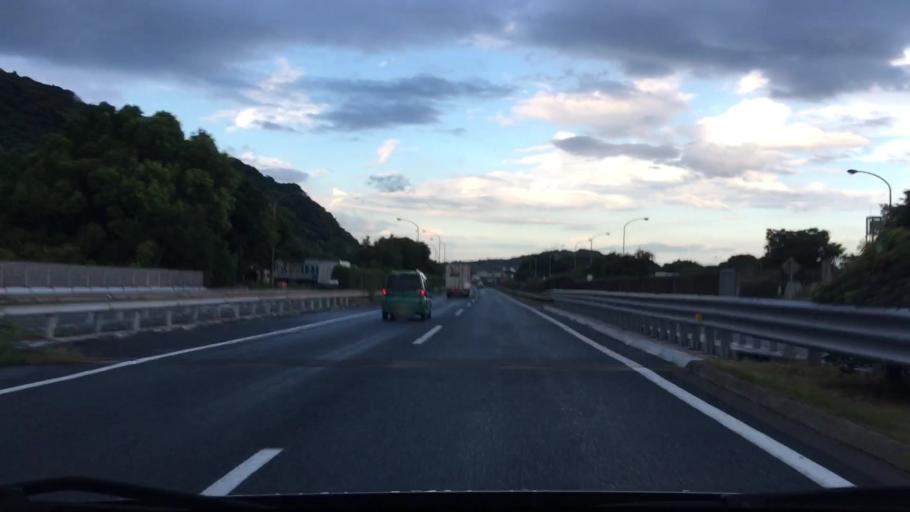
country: JP
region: Yamaguchi
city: Shimonoseki
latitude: 33.8711
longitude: 130.9627
